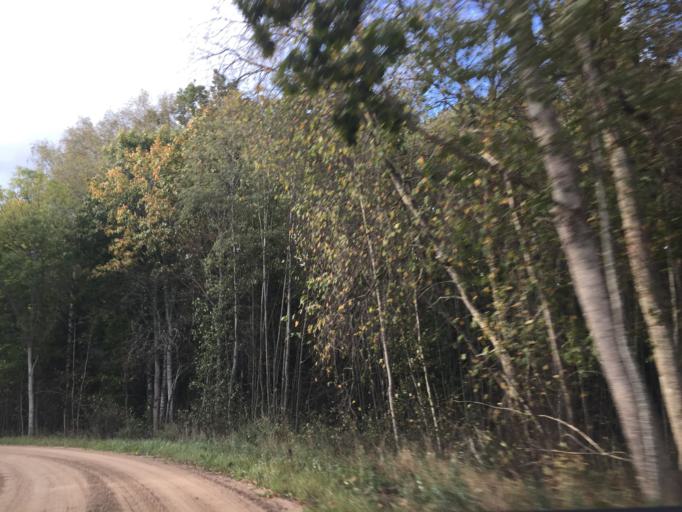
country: LV
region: Ligatne
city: Ligatne
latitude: 57.1355
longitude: 25.0952
